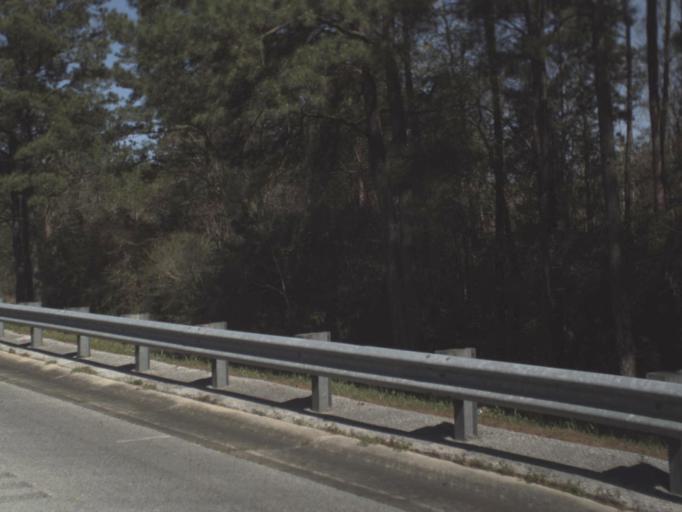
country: US
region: Florida
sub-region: Walton County
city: DeFuniak Springs
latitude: 30.7264
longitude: -86.2090
